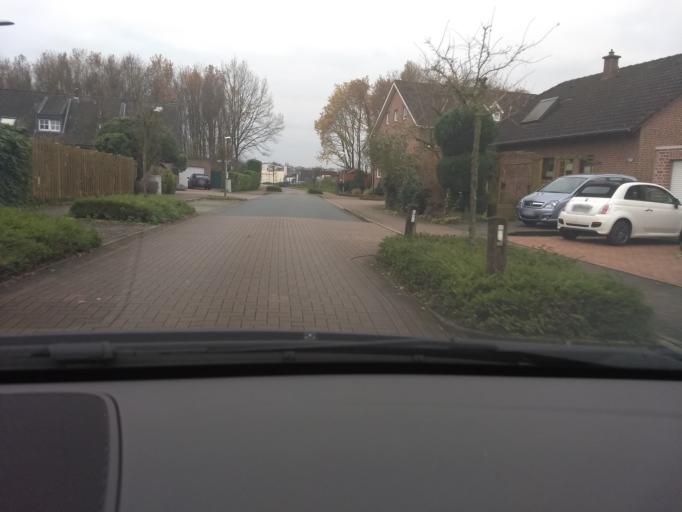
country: DE
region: North Rhine-Westphalia
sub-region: Regierungsbezirk Munster
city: Borken
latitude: 51.8582
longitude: 6.8724
